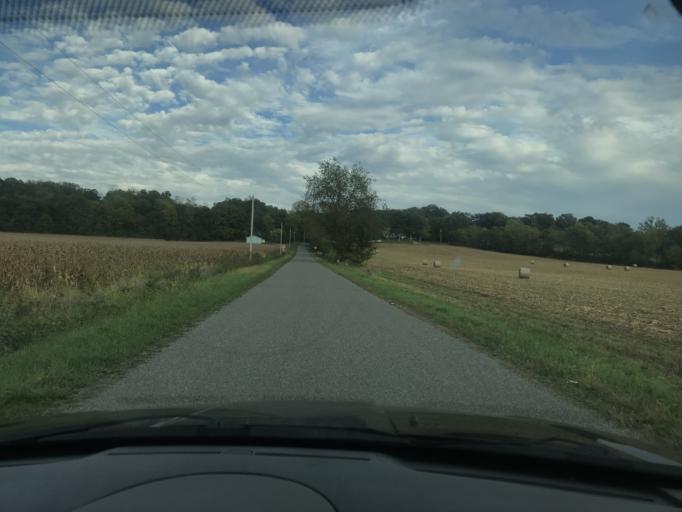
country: US
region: Ohio
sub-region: Logan County
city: West Liberty
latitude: 40.2478
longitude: -83.6941
